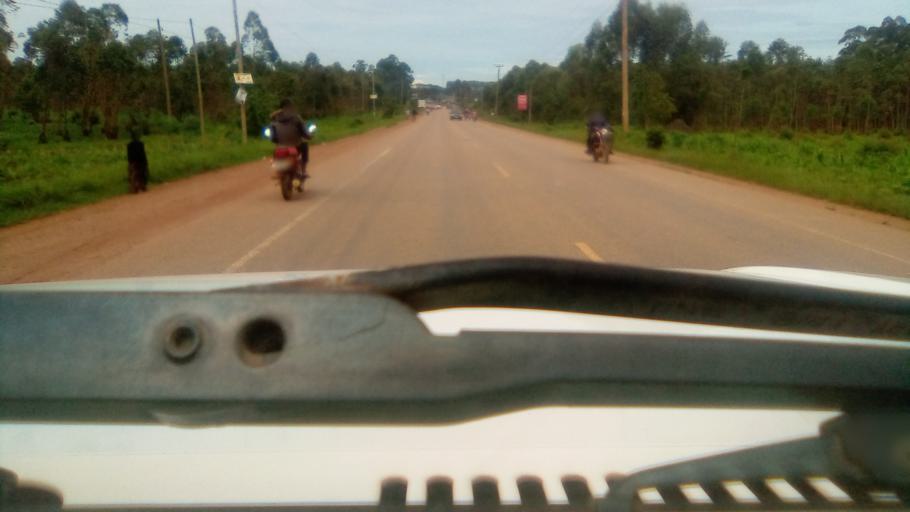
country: UG
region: Eastern Region
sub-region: Mbale District
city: Mbale
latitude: 1.0550
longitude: 34.1795
